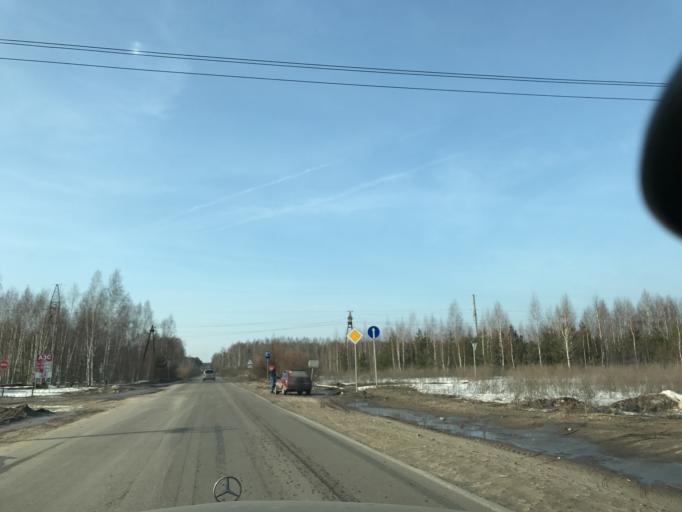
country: RU
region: Nizjnij Novgorod
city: Taremskoye
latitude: 55.9994
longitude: 43.0010
